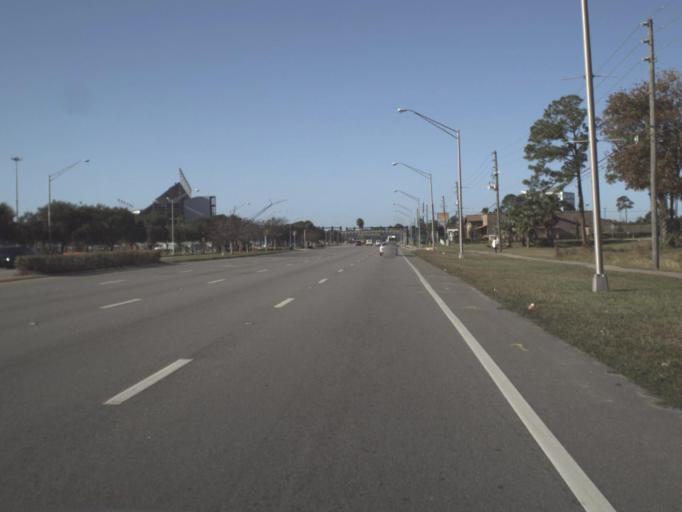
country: US
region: Florida
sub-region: Volusia County
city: Daytona Beach
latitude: 29.1944
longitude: -81.0635
